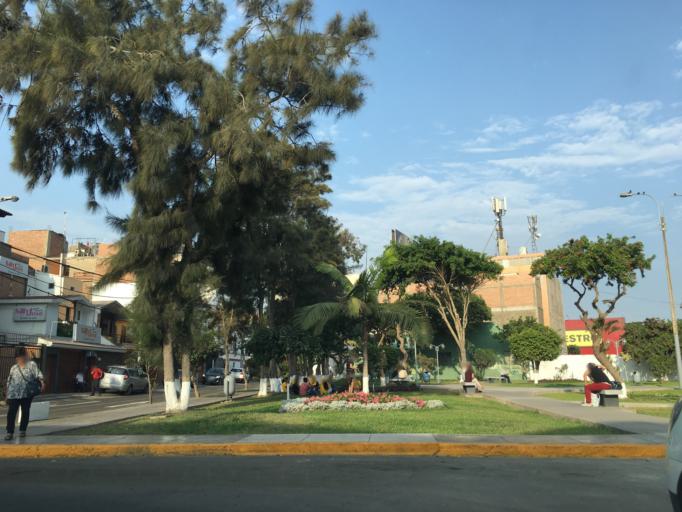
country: PE
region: Callao
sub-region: Callao
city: Callao
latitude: -12.0755
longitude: -77.0815
